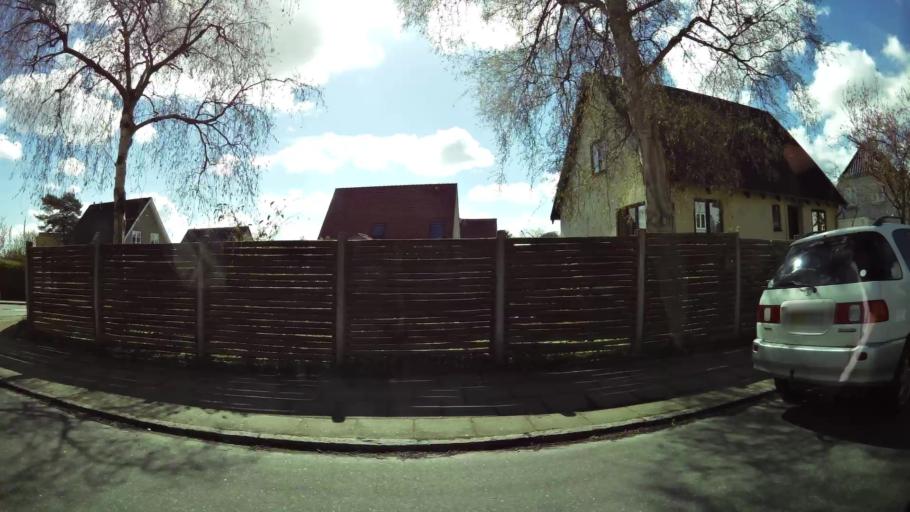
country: DK
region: North Denmark
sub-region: Alborg Kommune
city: Aalborg
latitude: 57.0374
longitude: 9.9012
